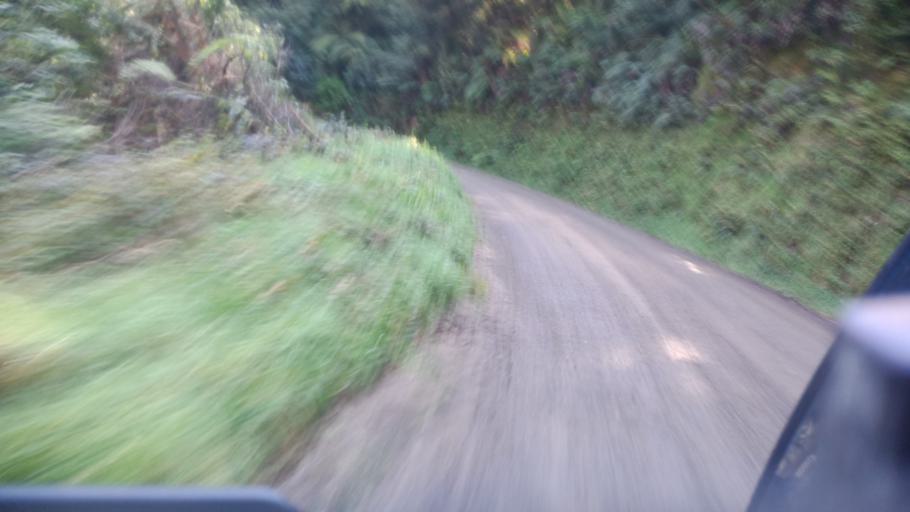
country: NZ
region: Bay of Plenty
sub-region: Opotiki District
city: Opotiki
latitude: -38.0512
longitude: 177.4552
